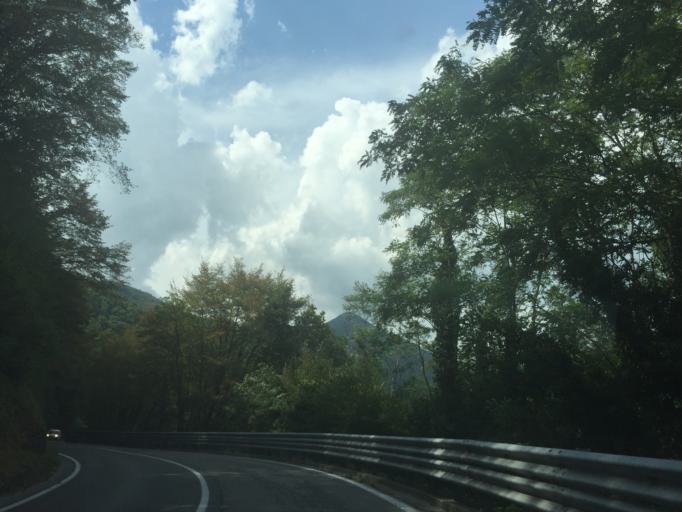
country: IT
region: Tuscany
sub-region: Provincia di Pistoia
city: Cutigliano
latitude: 44.0947
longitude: 10.7569
